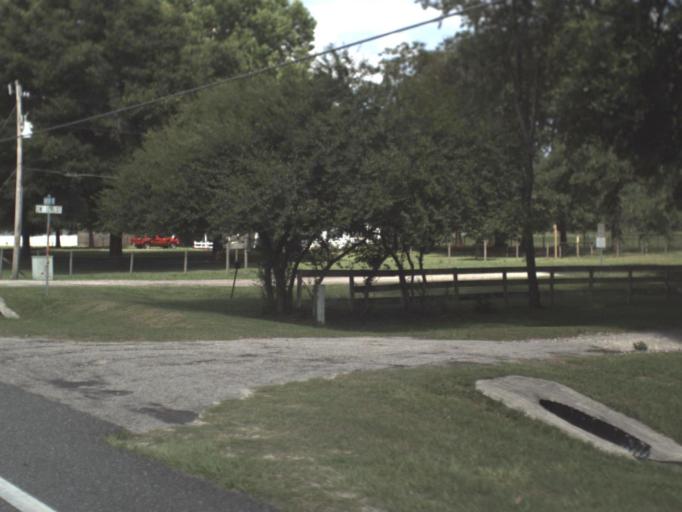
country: US
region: Florida
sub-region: Alachua County
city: Archer
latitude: 29.5633
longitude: -82.4793
